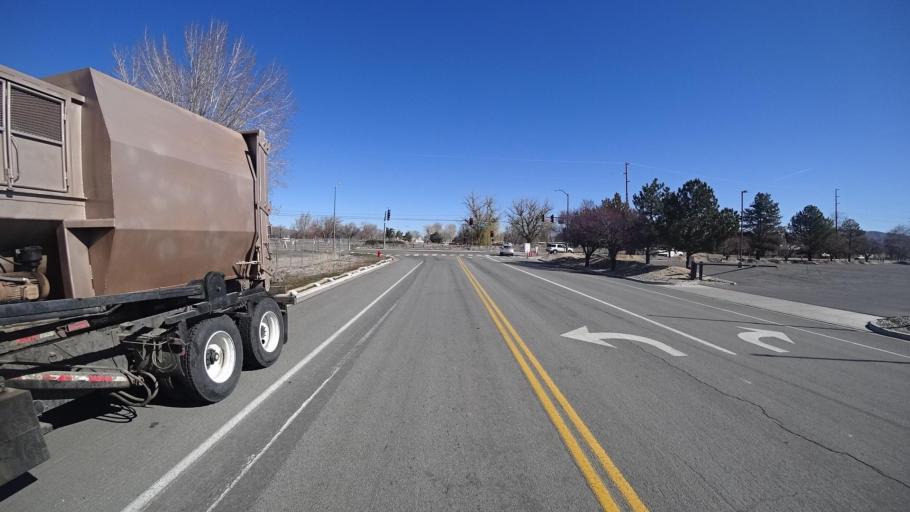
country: US
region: Nevada
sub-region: Washoe County
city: Sparks
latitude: 39.5135
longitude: -119.7523
